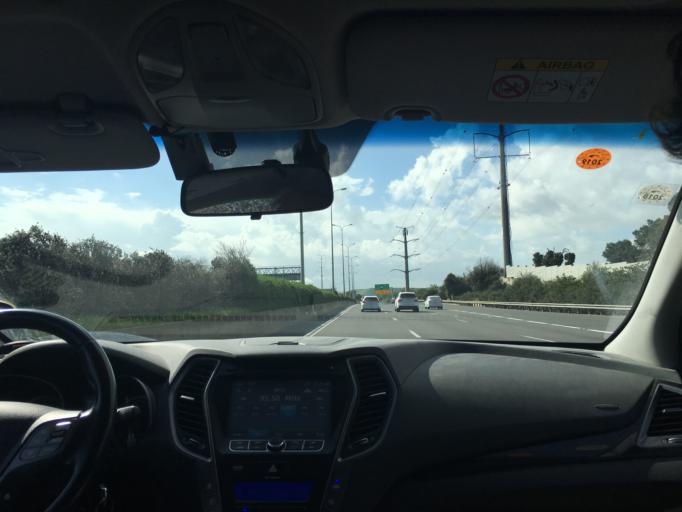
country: IL
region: Tel Aviv
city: Giv`atayim
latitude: 32.0500
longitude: 34.8313
